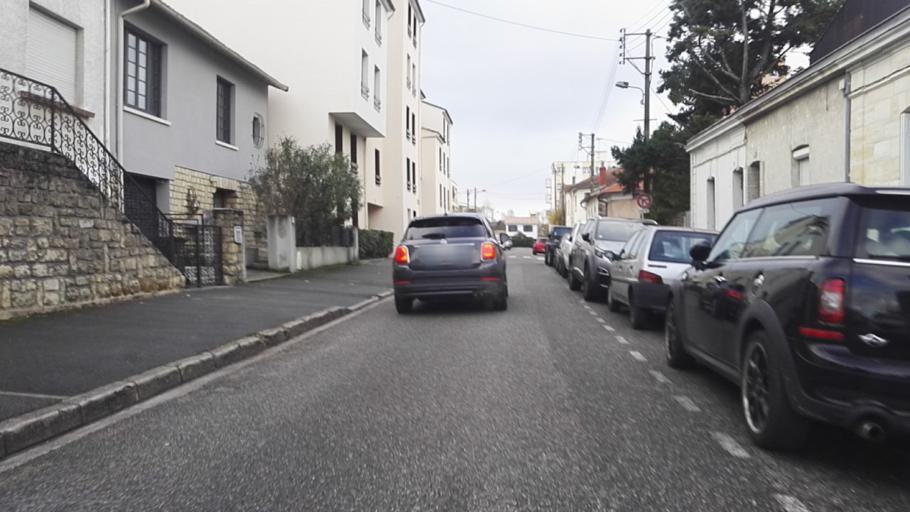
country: FR
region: Aquitaine
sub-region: Departement de la Gironde
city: Le Bouscat
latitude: 44.8471
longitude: -0.6091
